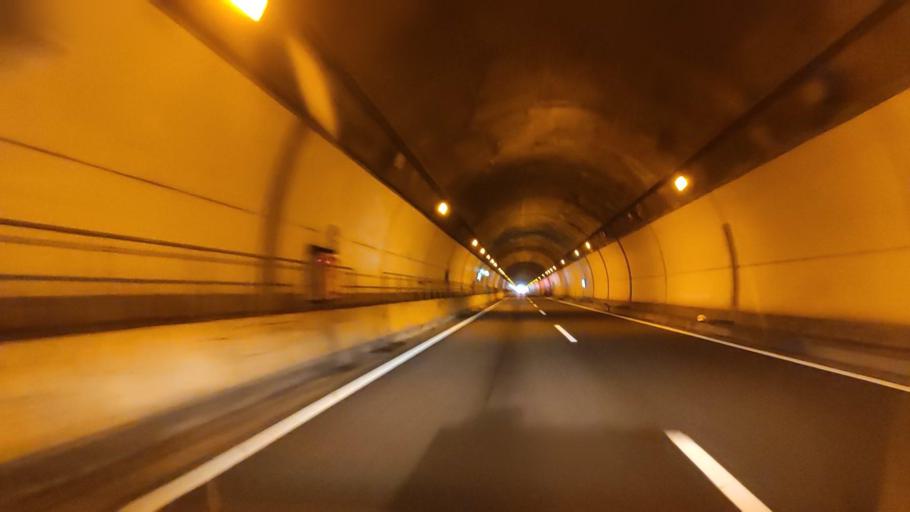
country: JP
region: Akita
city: Hanawa
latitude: 40.0098
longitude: 140.9887
